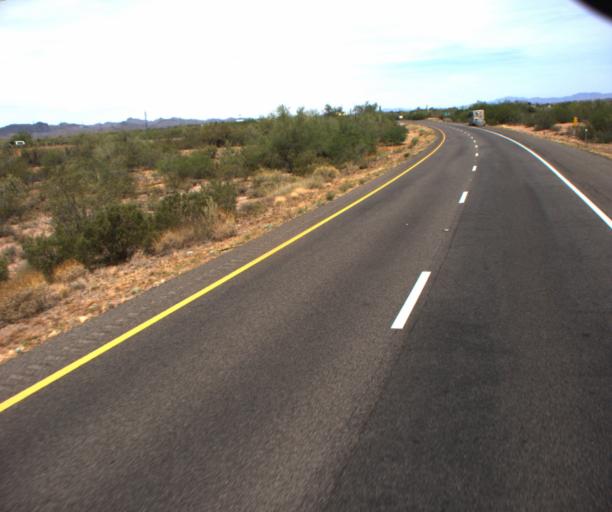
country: US
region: Arizona
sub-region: Maricopa County
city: Wickenburg
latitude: 33.8461
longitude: -112.6123
